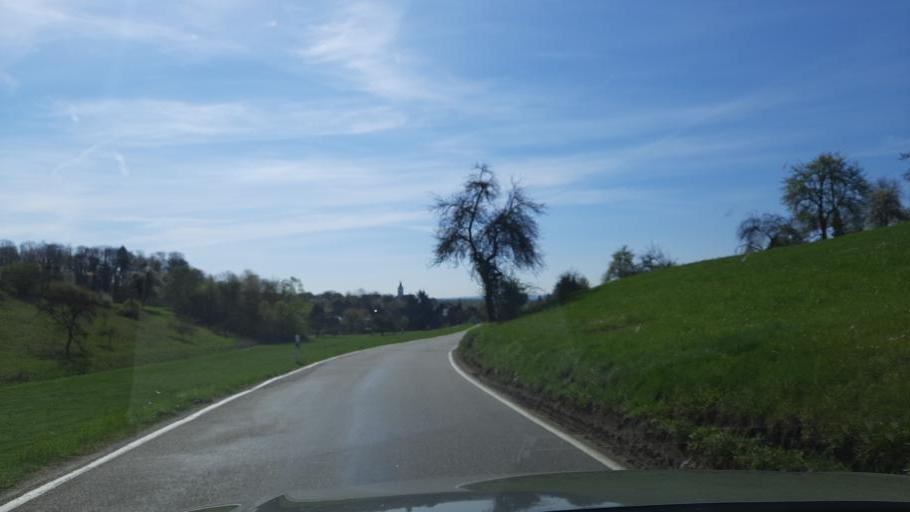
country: DE
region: Baden-Wuerttemberg
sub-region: Regierungsbezirk Stuttgart
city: Widdern
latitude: 49.2703
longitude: 9.3935
